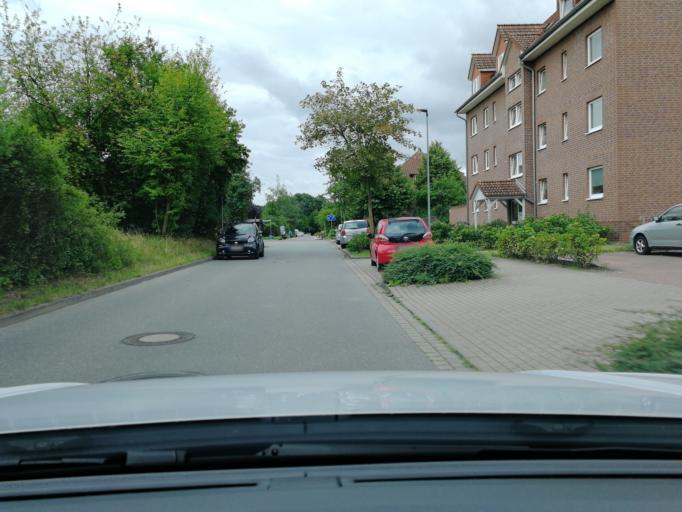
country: DE
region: Schleswig-Holstein
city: Schwarzenbek
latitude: 53.5101
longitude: 10.4790
